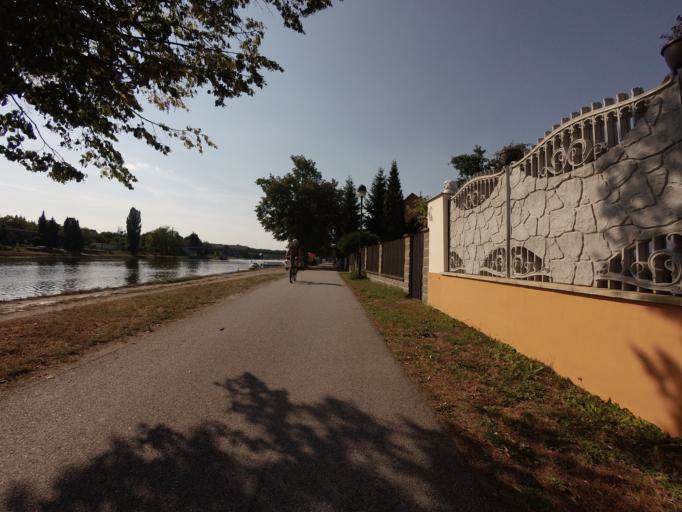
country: CZ
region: Jihocesky
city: Tyn nad Vltavou
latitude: 49.2201
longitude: 14.4247
